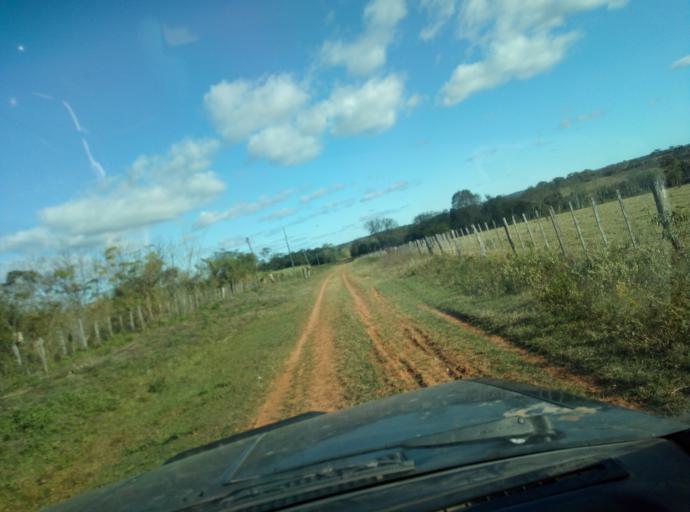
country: PY
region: Caaguazu
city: Doctor Cecilio Baez
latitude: -25.1657
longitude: -56.2726
